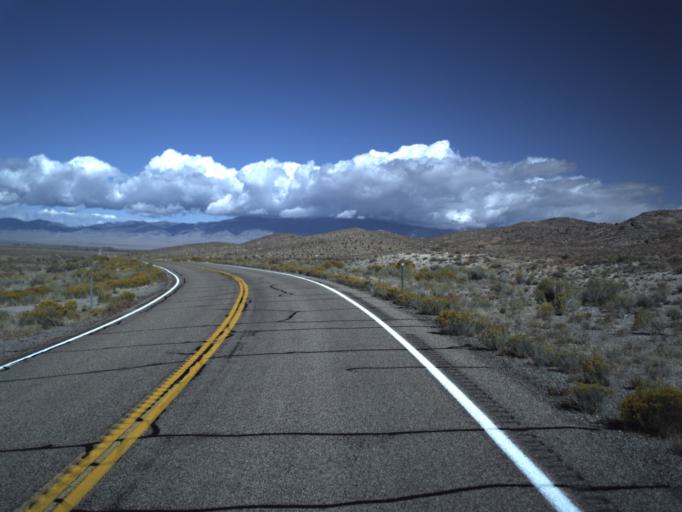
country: US
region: Nevada
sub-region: White Pine County
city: McGill
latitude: 38.8987
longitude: -114.0130
